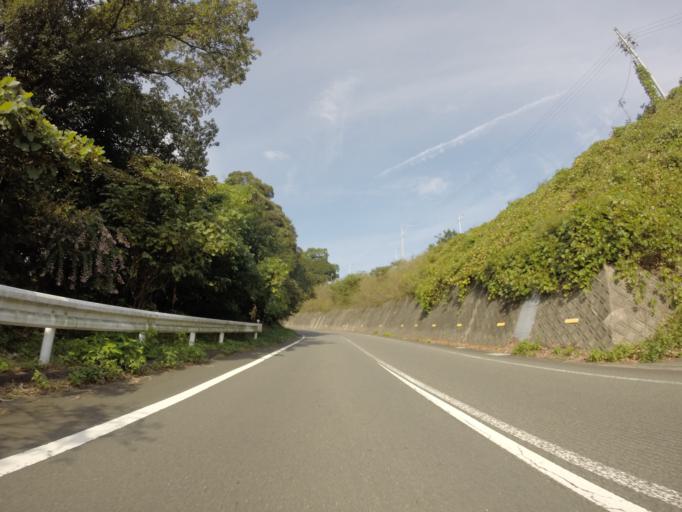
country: JP
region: Shizuoka
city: Shimada
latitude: 34.7690
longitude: 138.1712
